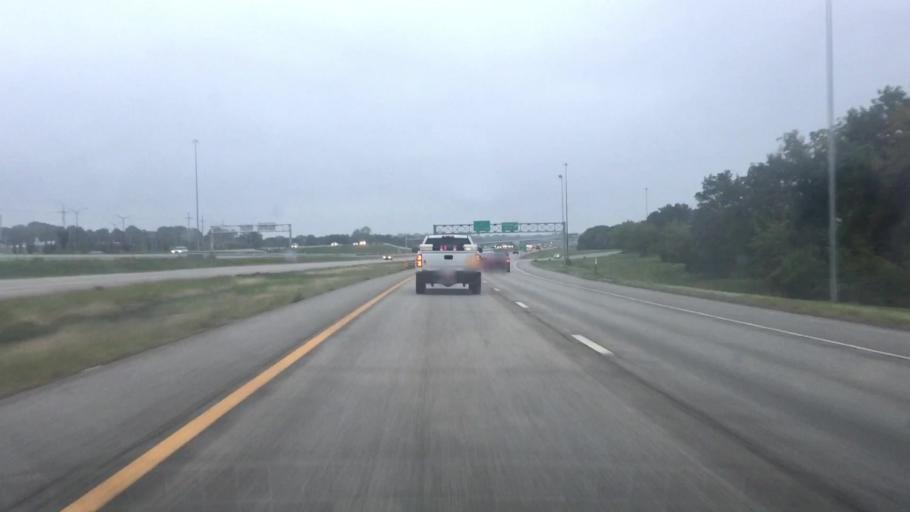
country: US
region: Kansas
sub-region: Johnson County
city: Lenexa
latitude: 38.9216
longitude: -94.7041
